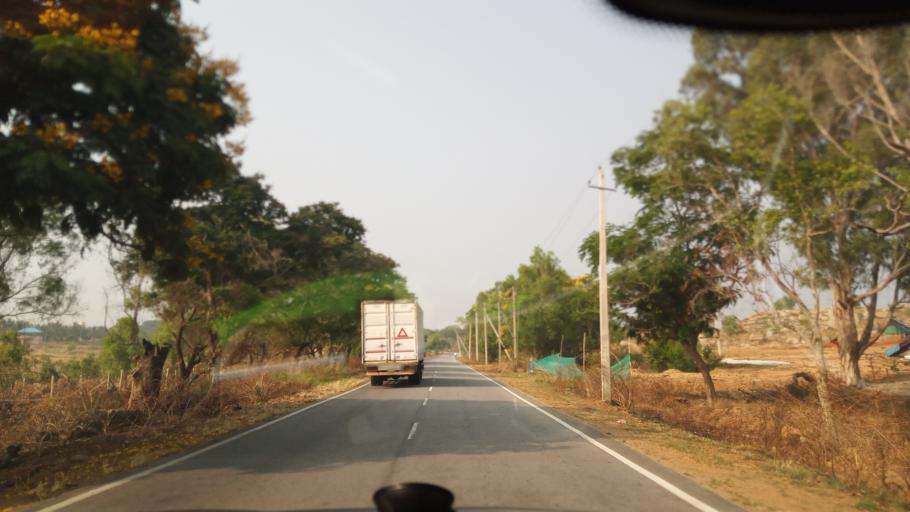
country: IN
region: Karnataka
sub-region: Mandya
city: Belluru
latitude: 12.9514
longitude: 76.7532
